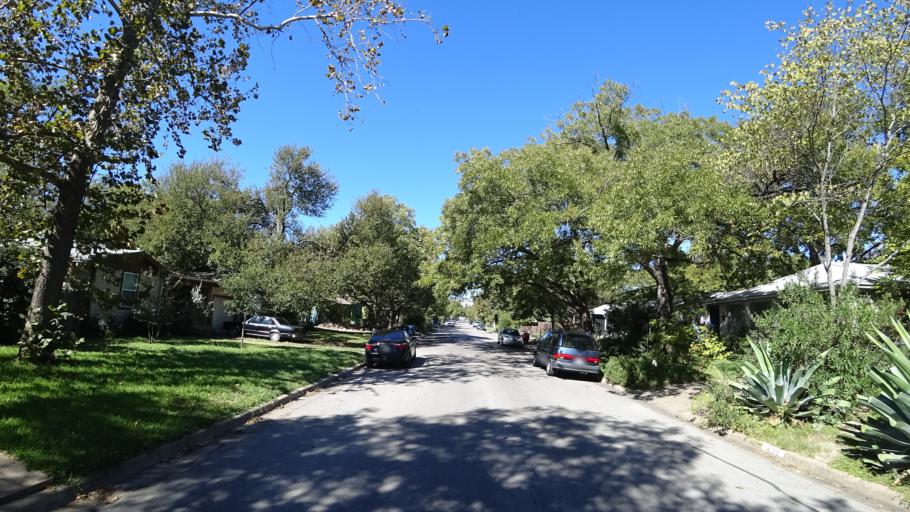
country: US
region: Texas
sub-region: Travis County
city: Austin
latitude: 30.3202
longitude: -97.7249
